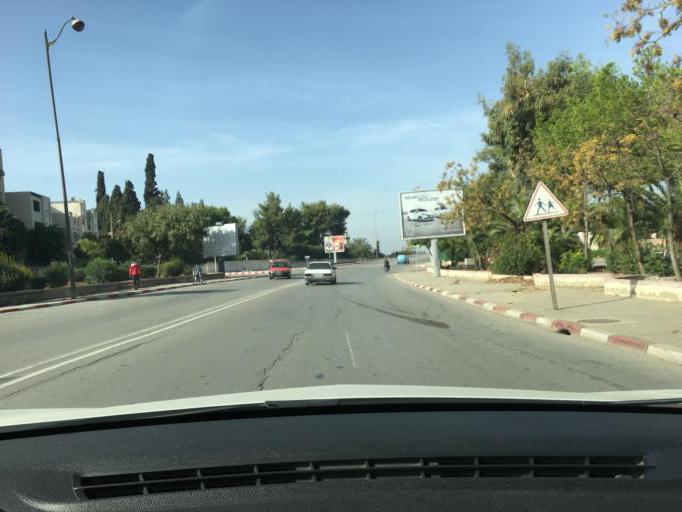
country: MA
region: Fes-Boulemane
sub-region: Fes
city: Fes
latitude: 34.0391
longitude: -5.0216
